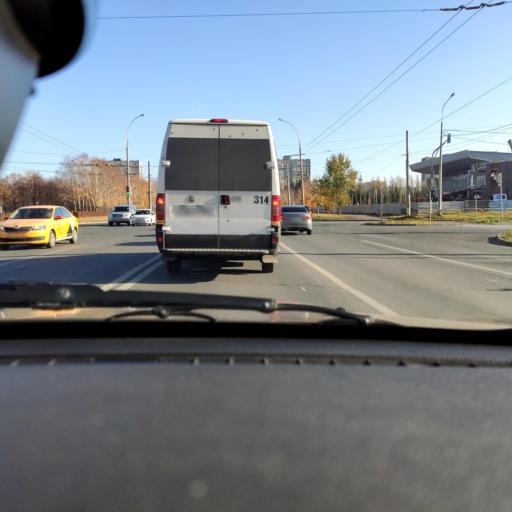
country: RU
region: Samara
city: Tol'yatti
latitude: 53.5072
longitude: 49.2702
